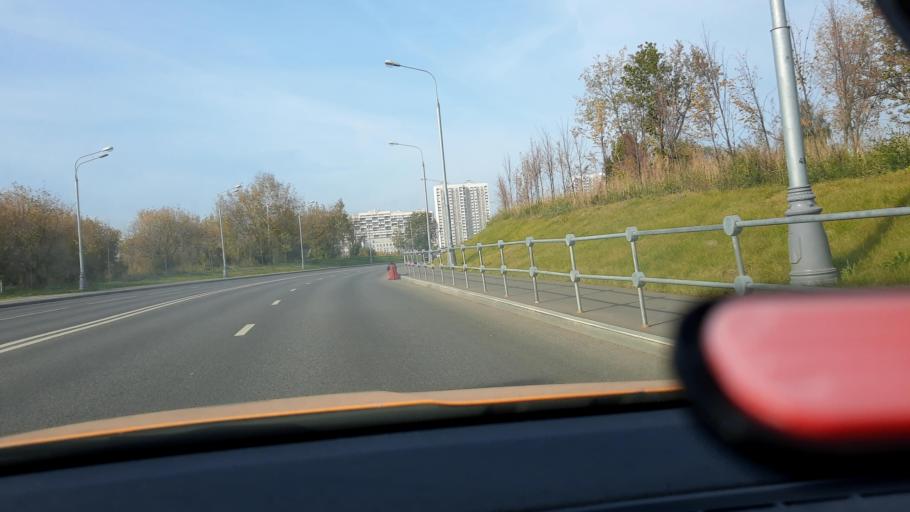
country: RU
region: Moscow
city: Ramenki
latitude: 55.6906
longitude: 37.5156
